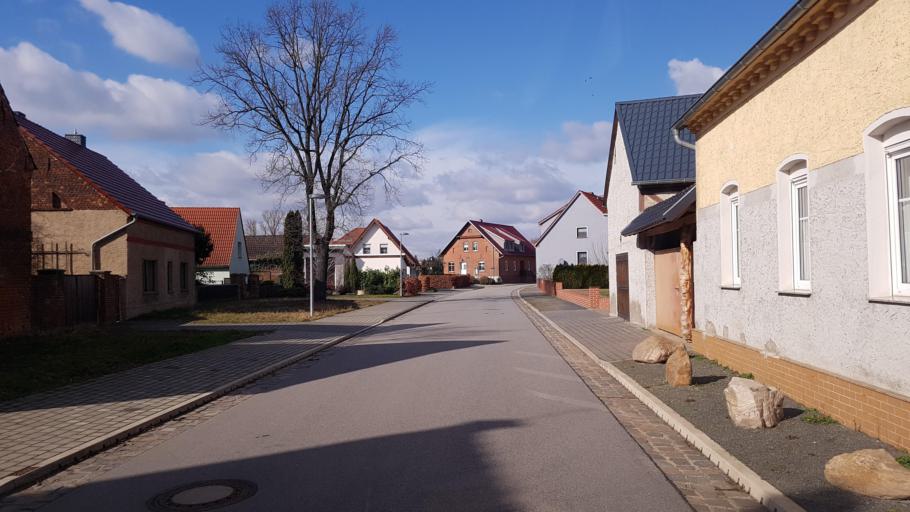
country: DE
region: Brandenburg
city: Herzberg
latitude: 51.6992
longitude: 13.2223
